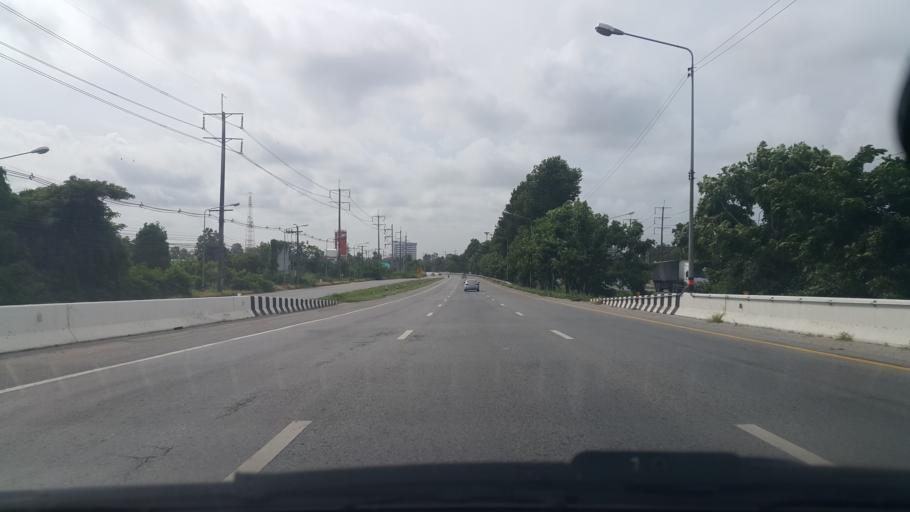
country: TH
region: Rayong
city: Rayong
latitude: 12.6854
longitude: 101.2985
